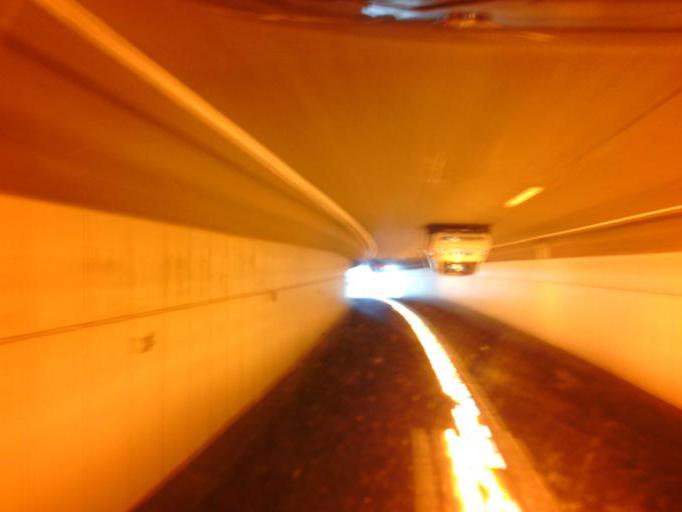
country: BE
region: Flanders
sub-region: Provincie Oost-Vlaanderen
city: Ledeberg
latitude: 51.0760
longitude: 3.7466
